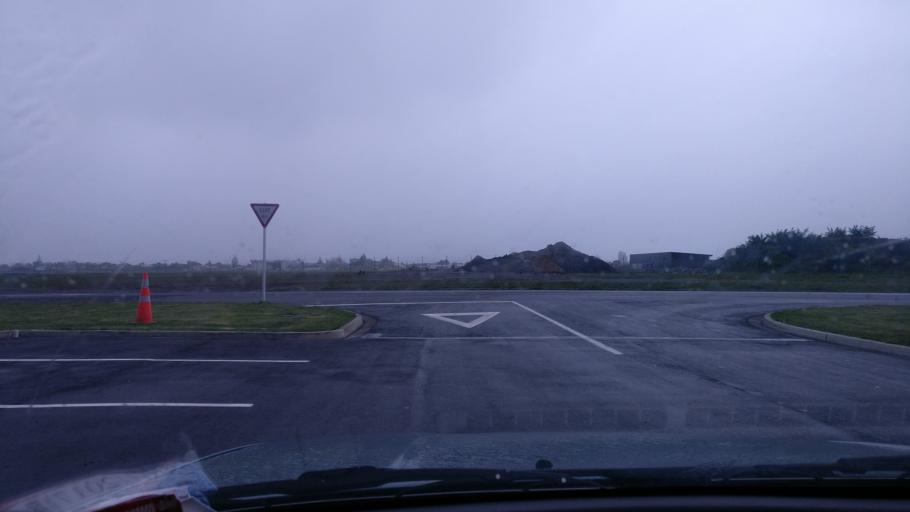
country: NZ
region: Wellington
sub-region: Kapiti Coast District
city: Paraparaumu
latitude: -40.9050
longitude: 174.9936
